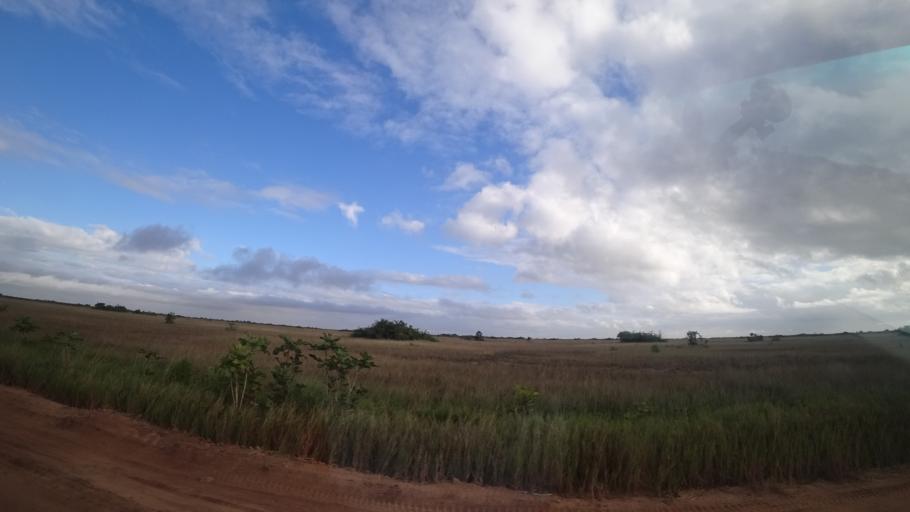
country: MZ
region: Sofala
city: Beira
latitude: -19.6963
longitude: 35.0330
